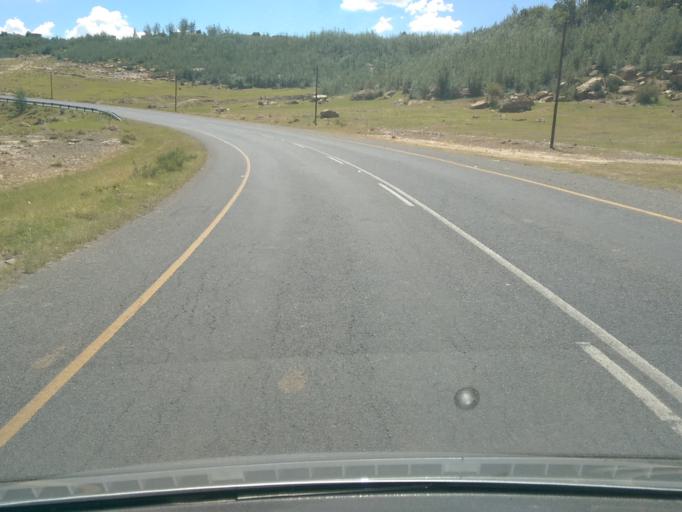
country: LS
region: Maseru
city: Maseru
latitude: -29.3948
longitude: 27.5293
